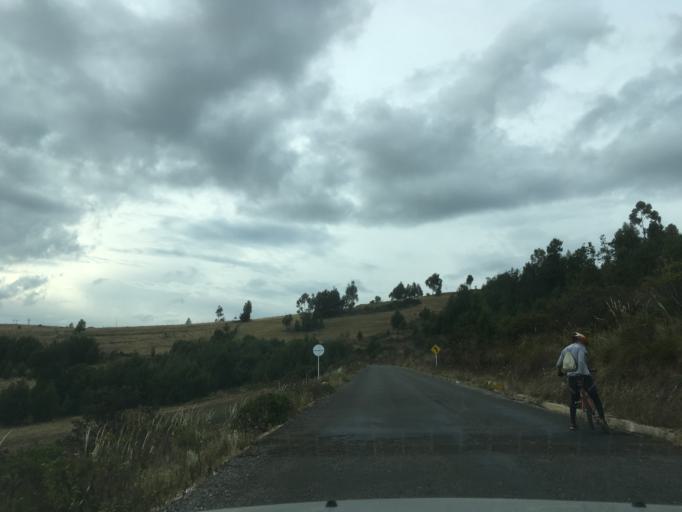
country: CO
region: Boyaca
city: Firavitoba
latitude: 5.6811
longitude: -73.0297
